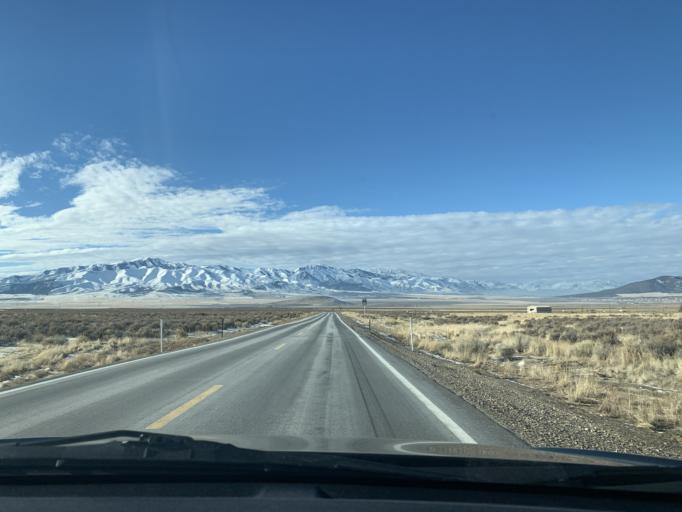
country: US
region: Utah
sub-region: Tooele County
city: Tooele
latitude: 40.3789
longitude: -112.3811
